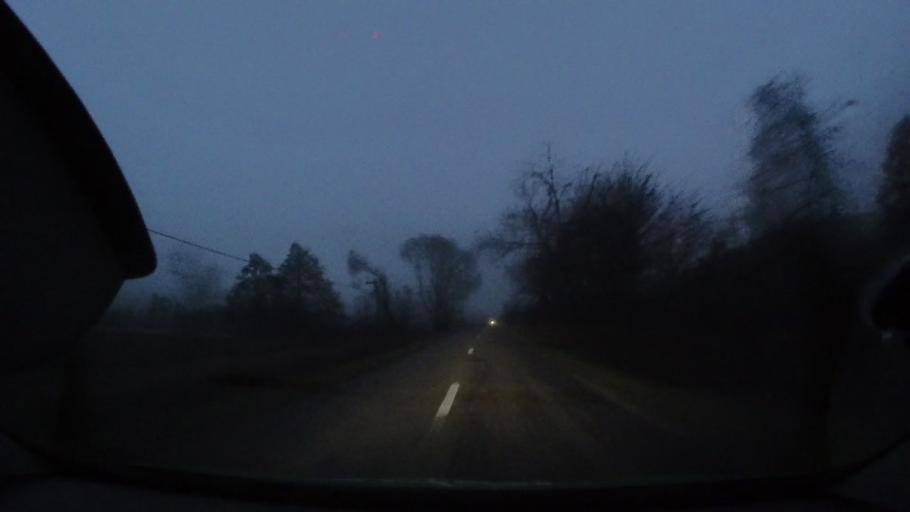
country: RO
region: Arad
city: Hatzmas
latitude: 46.5074
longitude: 22.0589
